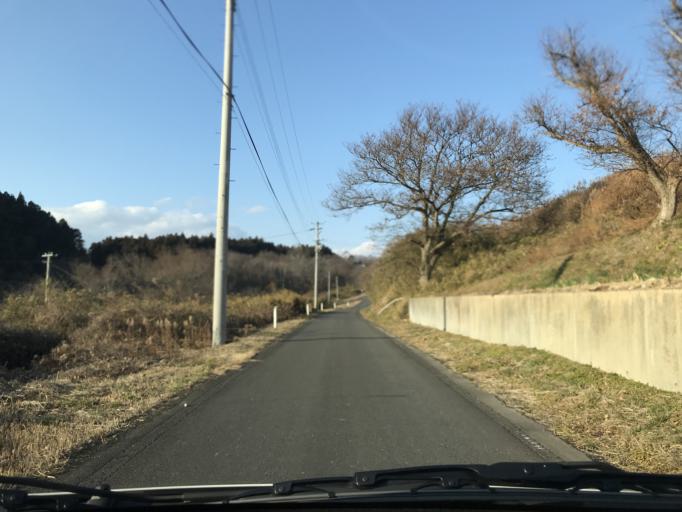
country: JP
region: Miyagi
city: Wakuya
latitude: 38.6914
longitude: 141.1059
